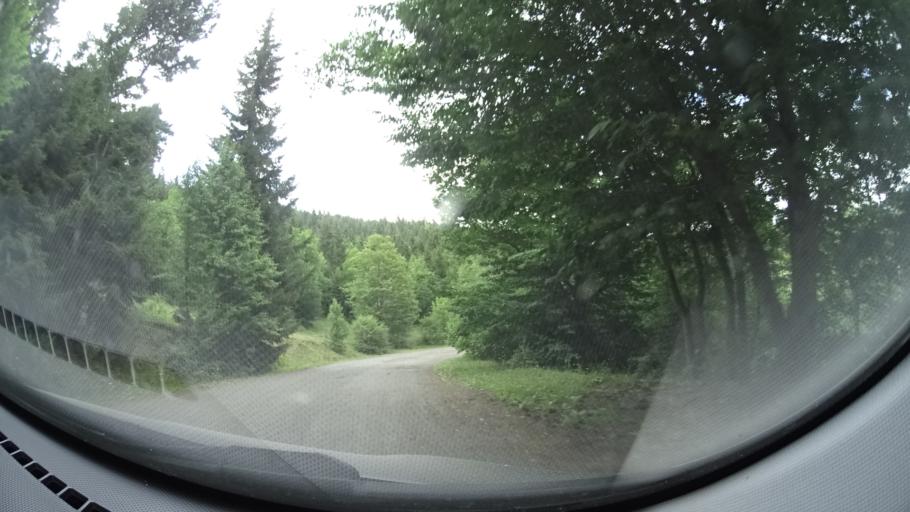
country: GE
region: Samtskhe-Javakheti
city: Adigeni
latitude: 41.6670
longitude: 42.6166
